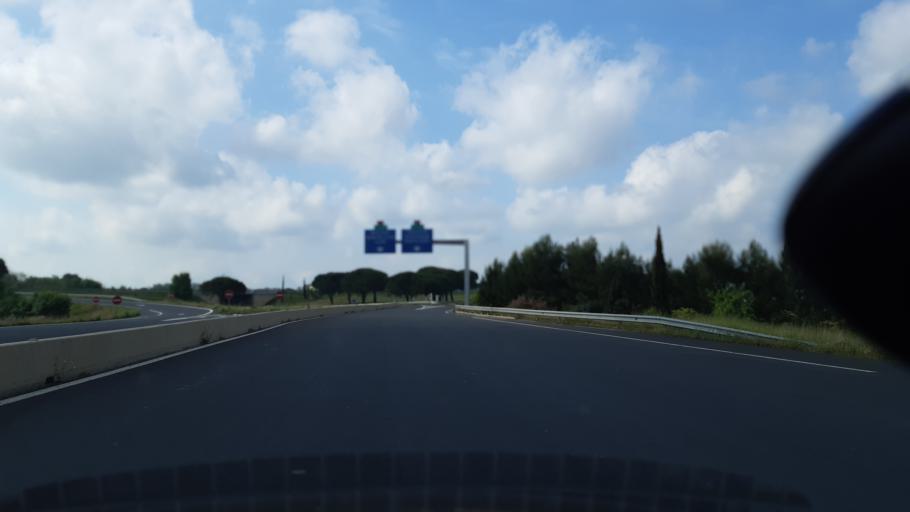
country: FR
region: Languedoc-Roussillon
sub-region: Departement de l'Aude
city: Narbonne
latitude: 43.1790
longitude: 3.0346
